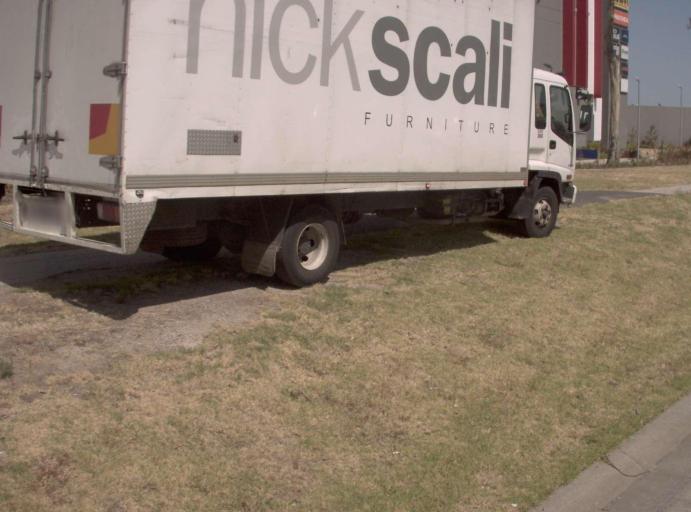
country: AU
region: Victoria
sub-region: Monash
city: Clayton
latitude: -37.9282
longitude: 145.1425
